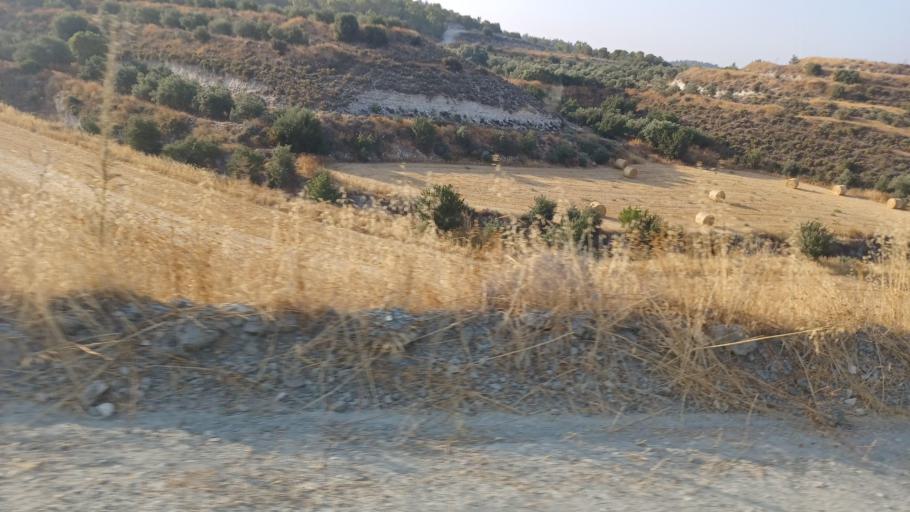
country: CY
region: Larnaka
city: Psevdas
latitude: 34.9390
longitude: 33.5047
